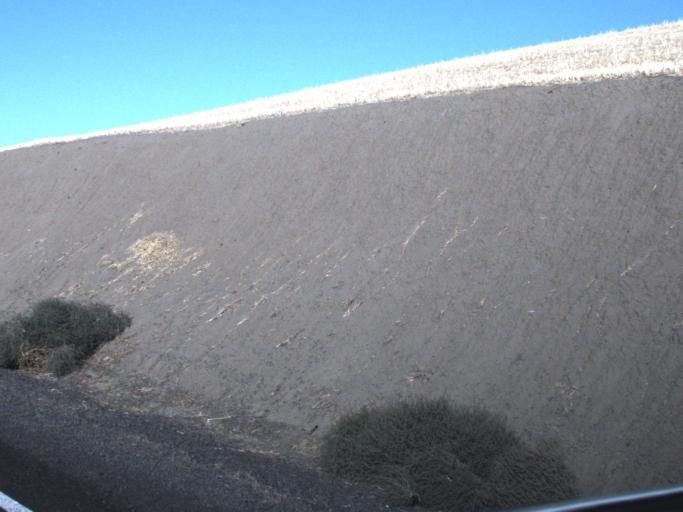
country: US
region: Washington
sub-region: Walla Walla County
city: Walla Walla
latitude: 46.1103
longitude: -118.3735
